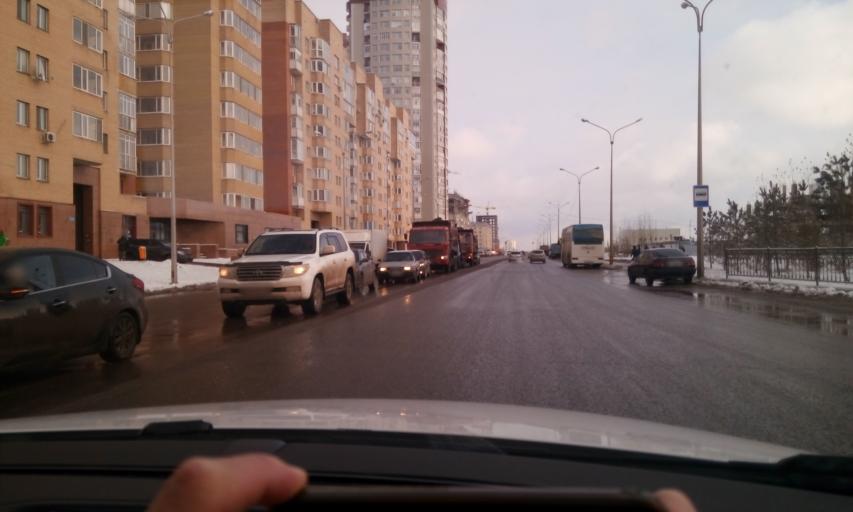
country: KZ
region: Astana Qalasy
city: Astana
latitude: 51.1236
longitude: 71.4759
